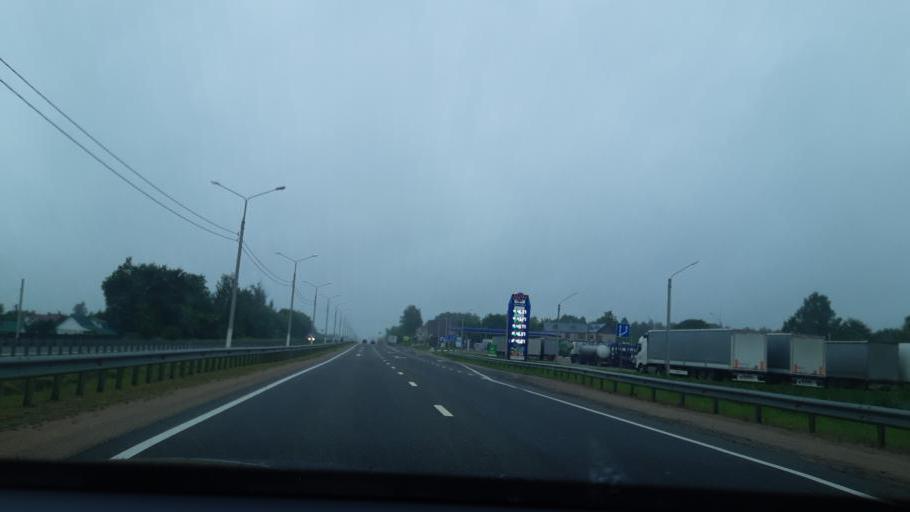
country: RU
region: Smolensk
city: Talashkino
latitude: 54.6465
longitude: 32.1718
